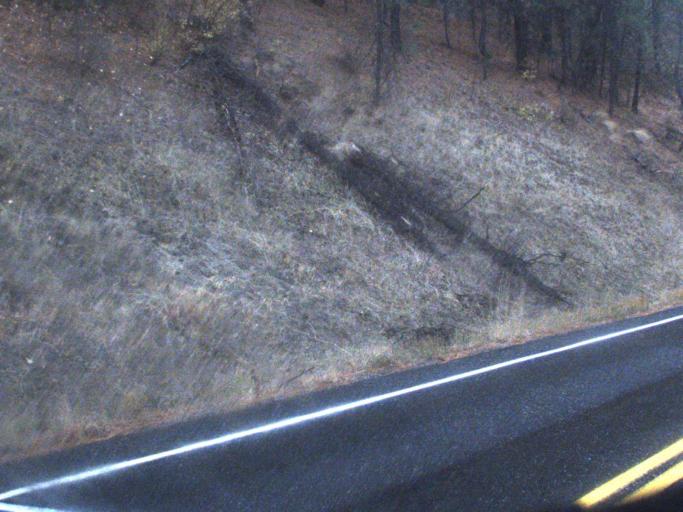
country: US
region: Washington
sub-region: Stevens County
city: Kettle Falls
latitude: 48.4939
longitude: -118.1620
